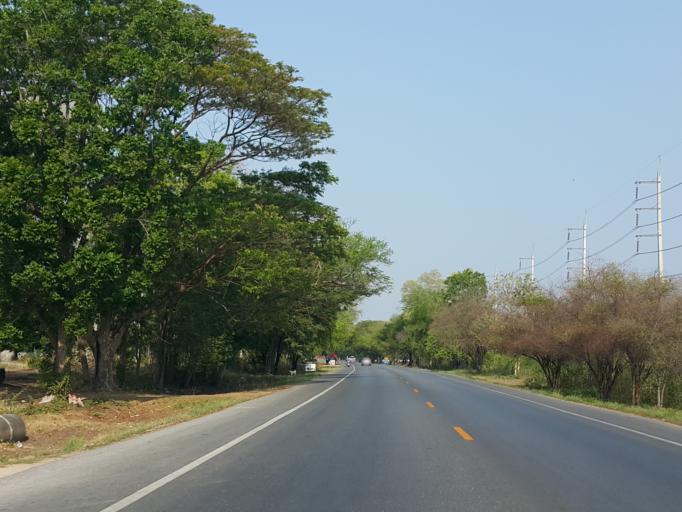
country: TH
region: Kanchanaburi
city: Sai Yok
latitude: 14.0899
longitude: 99.3139
